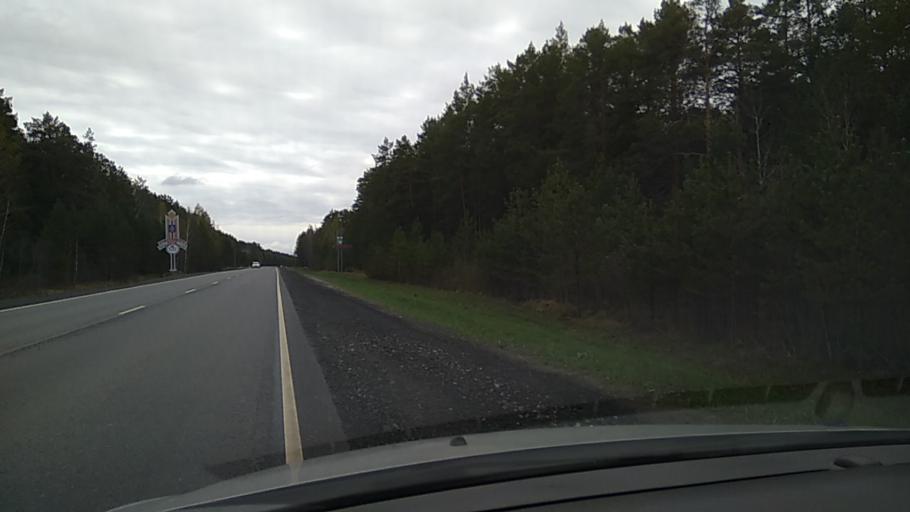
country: RU
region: Tjumen
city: Chervishevo
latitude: 56.8191
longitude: 65.3800
